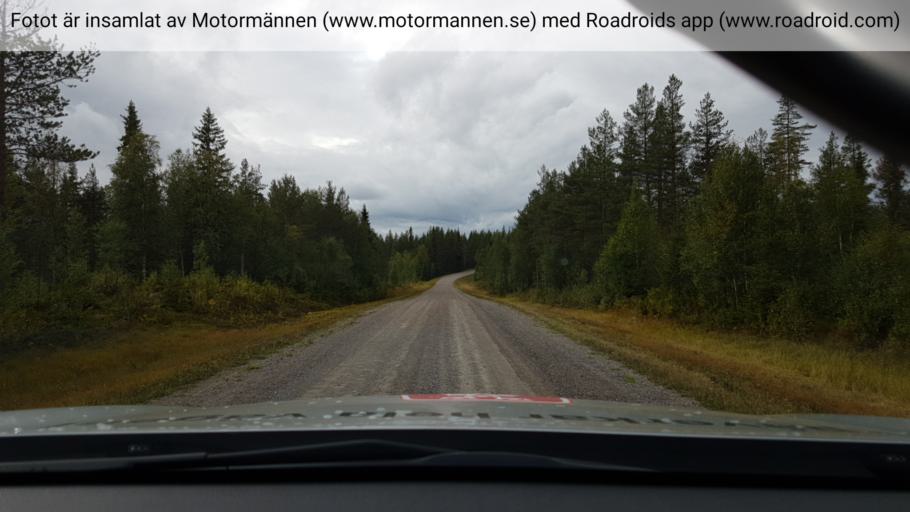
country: SE
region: Vaesterbotten
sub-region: Skelleftea Kommun
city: Langsele
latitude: 65.3375
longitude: 20.0033
